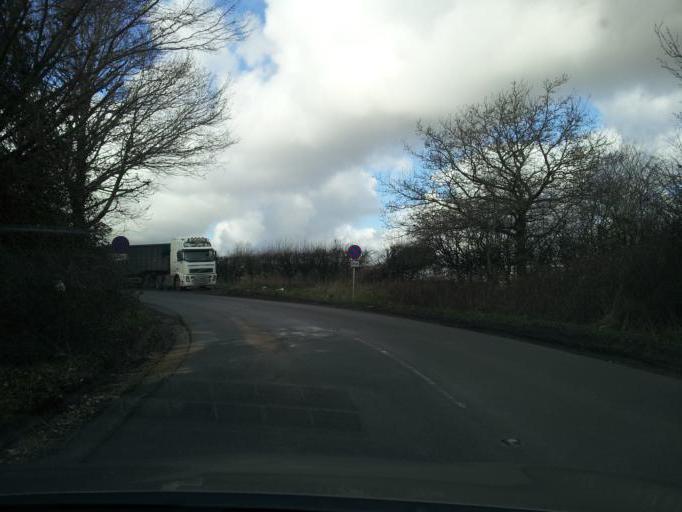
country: GB
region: England
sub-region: Norfolk
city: Mattishall
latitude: 52.6674
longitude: 1.1010
